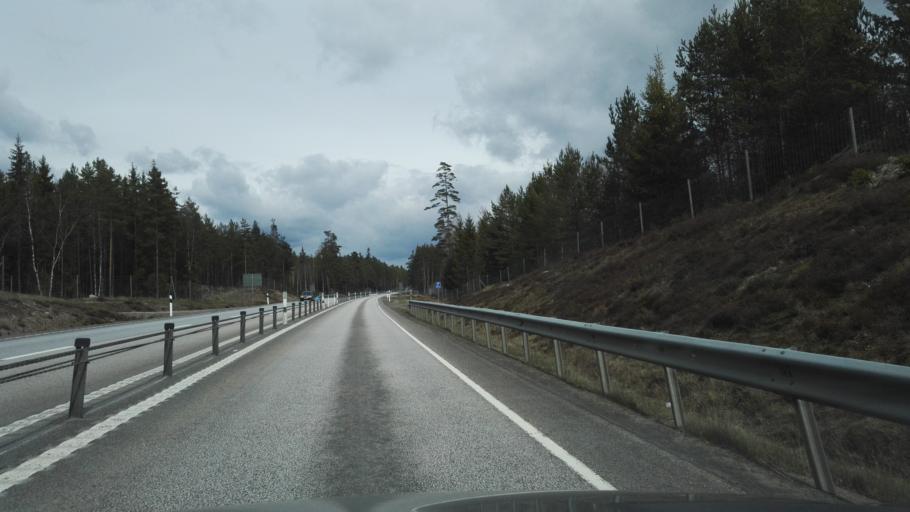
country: SE
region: Kronoberg
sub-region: Vaxjo Kommun
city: Braas
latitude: 56.9916
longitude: 14.9992
